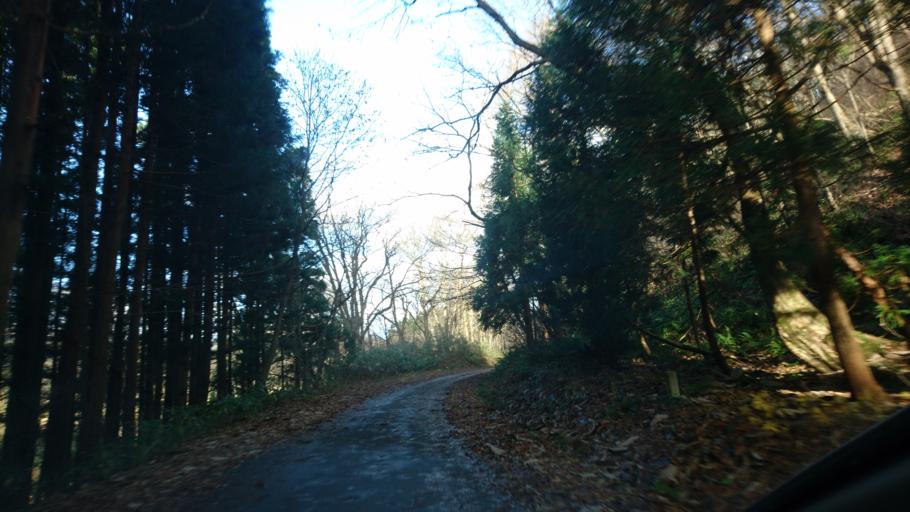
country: JP
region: Akita
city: Kakunodatemachi
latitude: 39.4792
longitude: 140.8053
